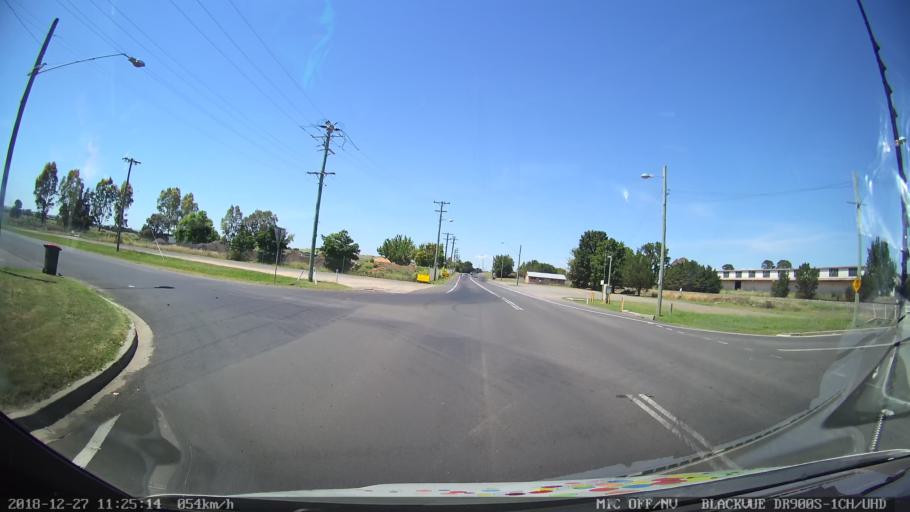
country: AU
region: New South Wales
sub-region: Bathurst Regional
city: Bathurst
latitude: -33.4398
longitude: 149.5786
